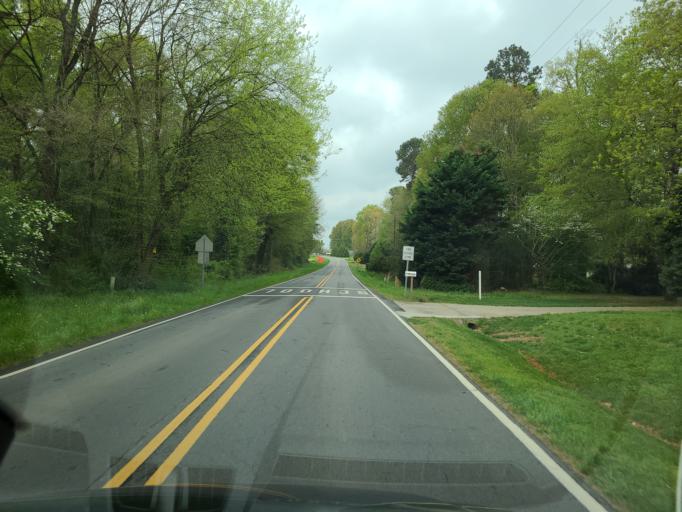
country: US
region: North Carolina
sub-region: Lincoln County
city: Lincolnton
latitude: 35.4637
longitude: -81.2920
